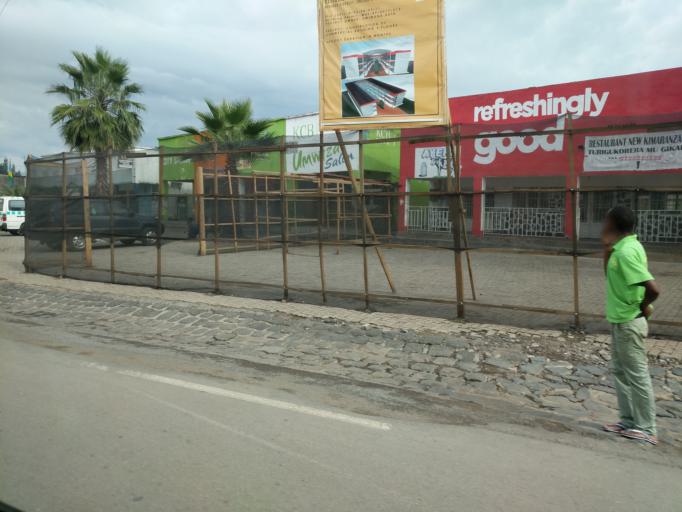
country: RW
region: Northern Province
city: Musanze
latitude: -1.5088
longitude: 29.6416
